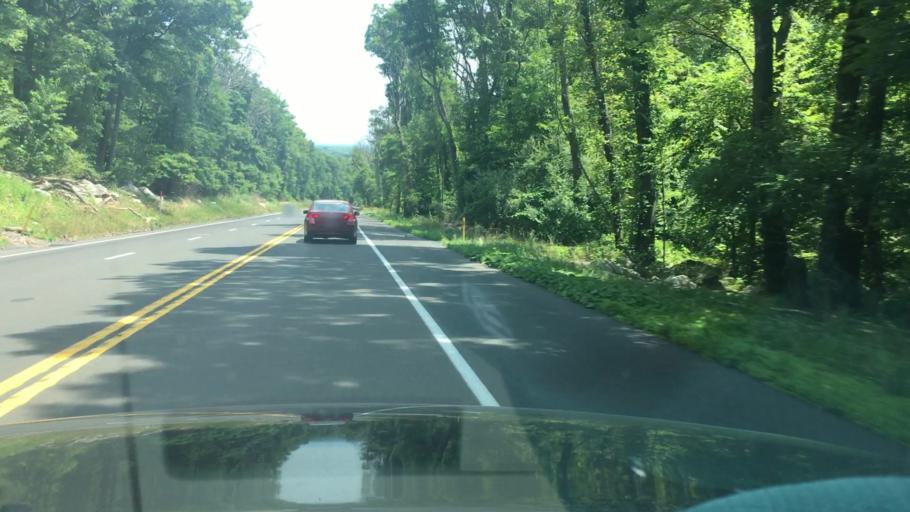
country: US
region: Pennsylvania
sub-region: Carbon County
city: Lehighton
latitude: 40.7161
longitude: -75.7827
